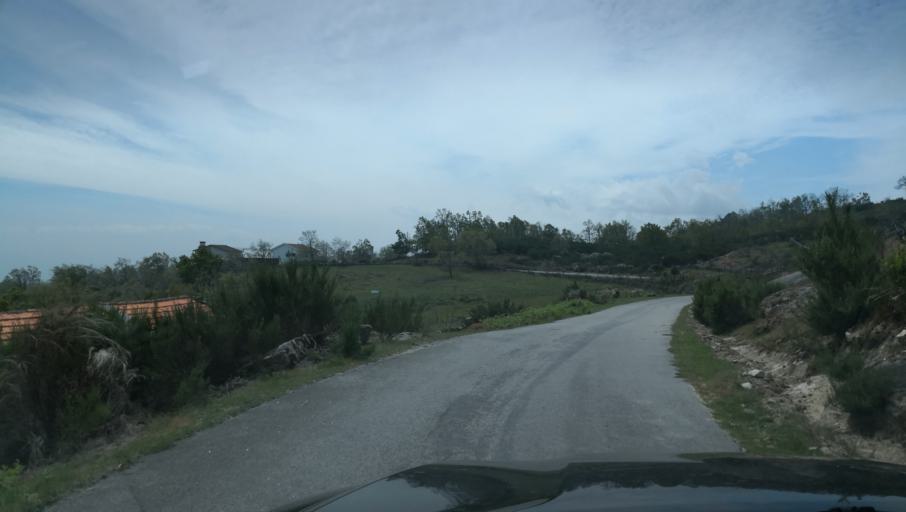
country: PT
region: Vila Real
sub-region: Vila Real
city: Vila Real
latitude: 41.2960
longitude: -7.8144
